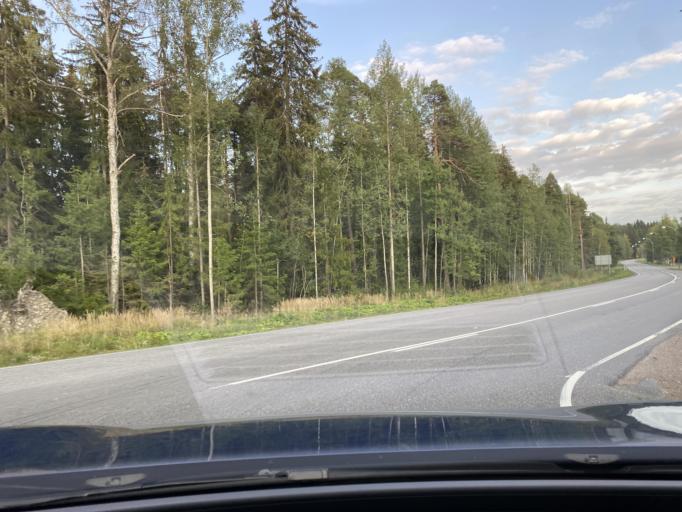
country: FI
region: Kymenlaakso
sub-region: Kouvola
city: Kouvola
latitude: 60.8976
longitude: 26.6674
